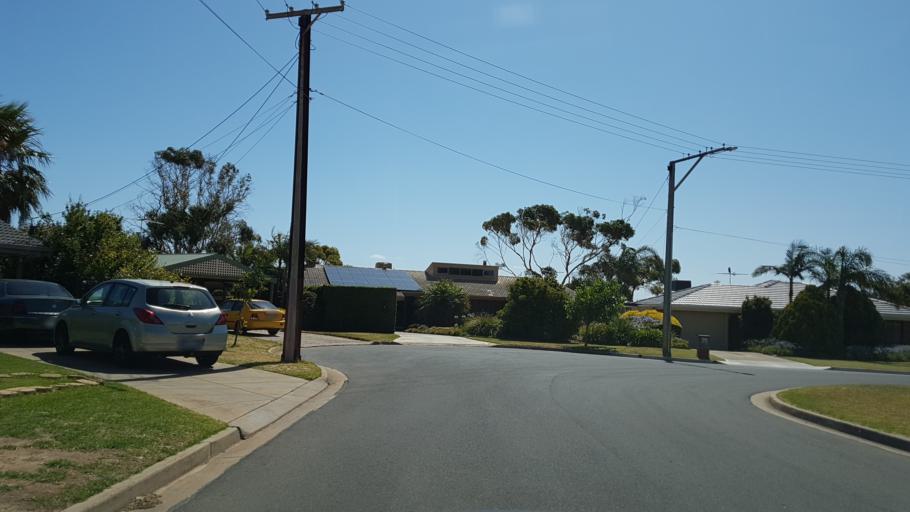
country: AU
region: South Australia
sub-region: Onkaparinga
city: Seaford
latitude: -35.1890
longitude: 138.4756
